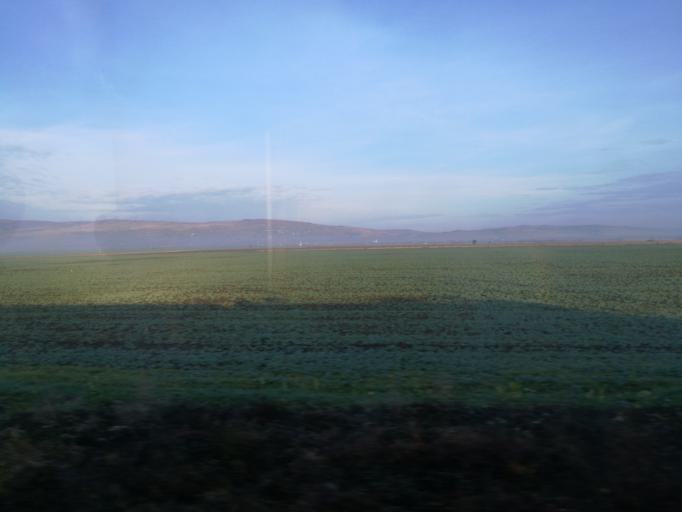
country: RO
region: Buzau
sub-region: Comuna Ulmeni
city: Ulmeni
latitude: 45.0891
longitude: 26.6719
